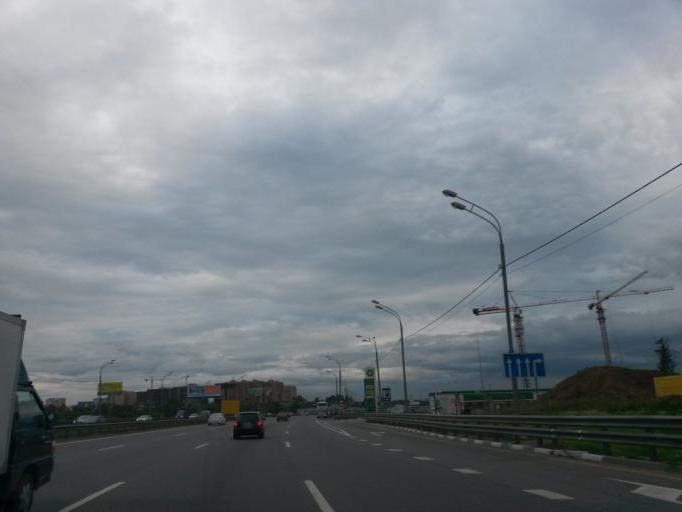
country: RU
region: Moscow
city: Biryulevo
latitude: 55.5687
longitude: 37.6926
